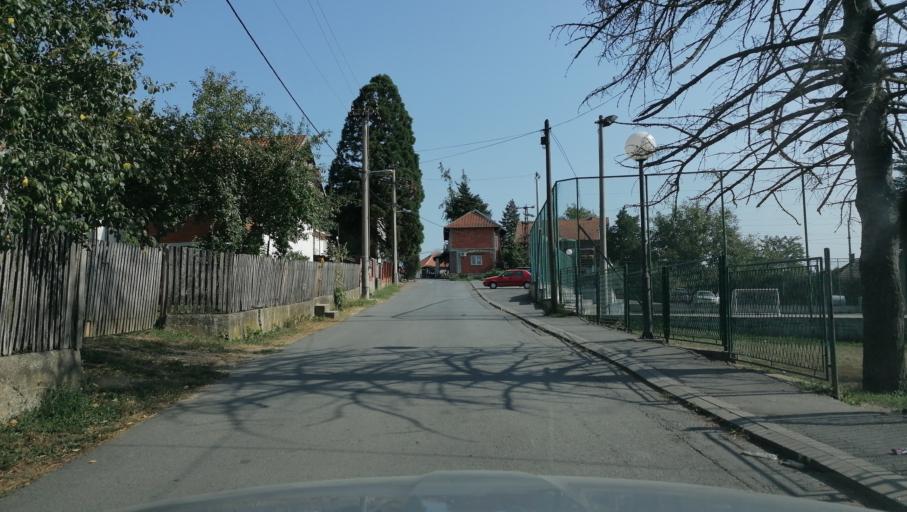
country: RS
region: Central Serbia
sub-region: Belgrade
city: Sopot
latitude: 44.5849
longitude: 20.6077
